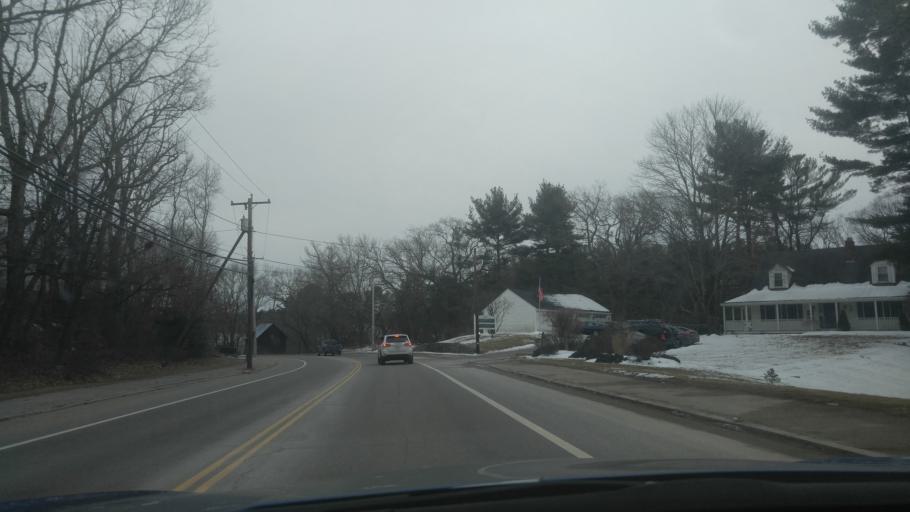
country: US
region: Rhode Island
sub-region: Kent County
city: West Warwick
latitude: 41.6917
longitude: -71.5707
